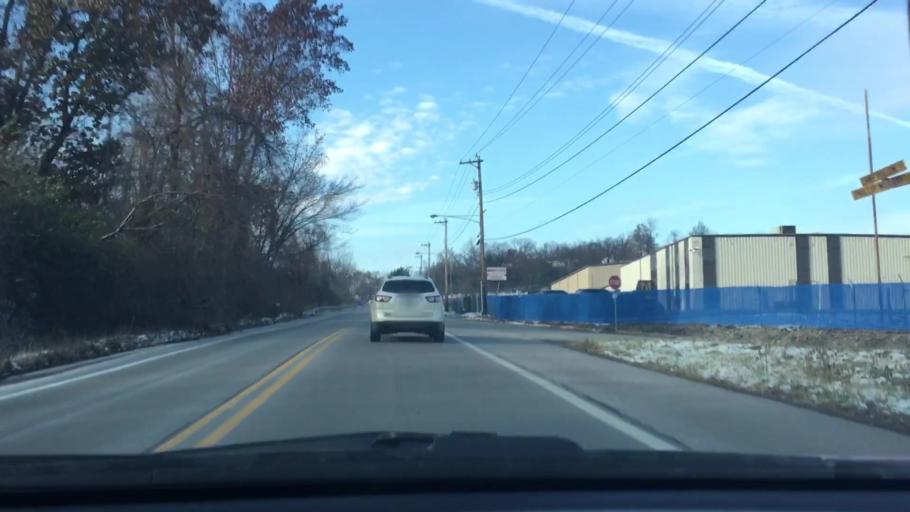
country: US
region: Pennsylvania
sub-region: Allegheny County
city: Glassport
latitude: 40.3389
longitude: -79.9131
